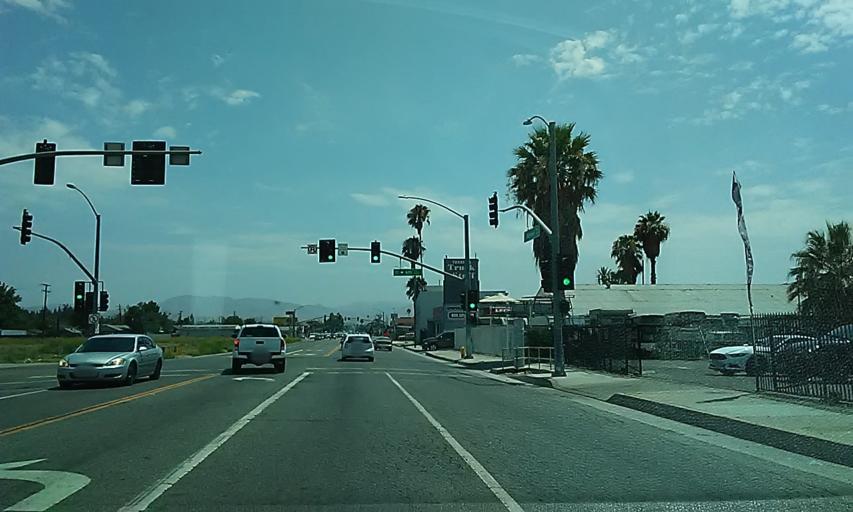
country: US
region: California
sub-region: San Bernardino County
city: San Bernardino
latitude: 34.1106
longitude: -117.2789
